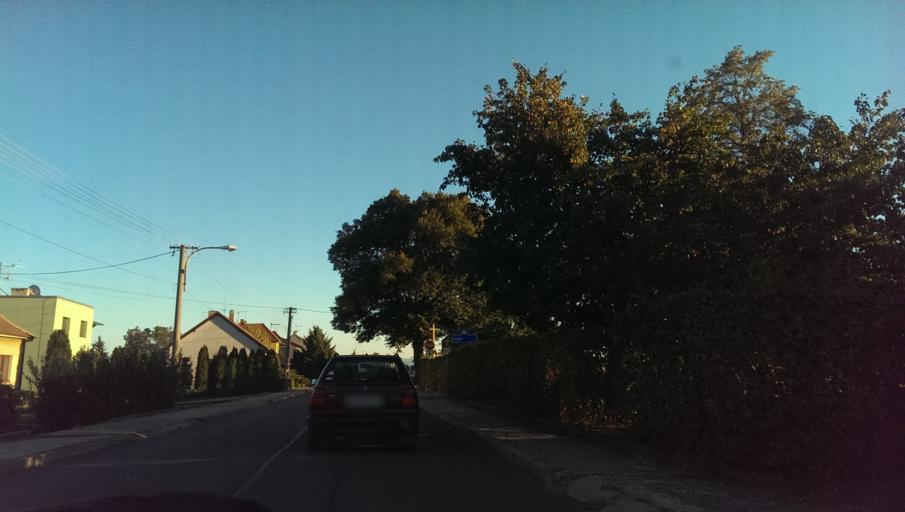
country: CZ
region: Zlin
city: Zlechov
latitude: 49.0791
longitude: 17.3771
